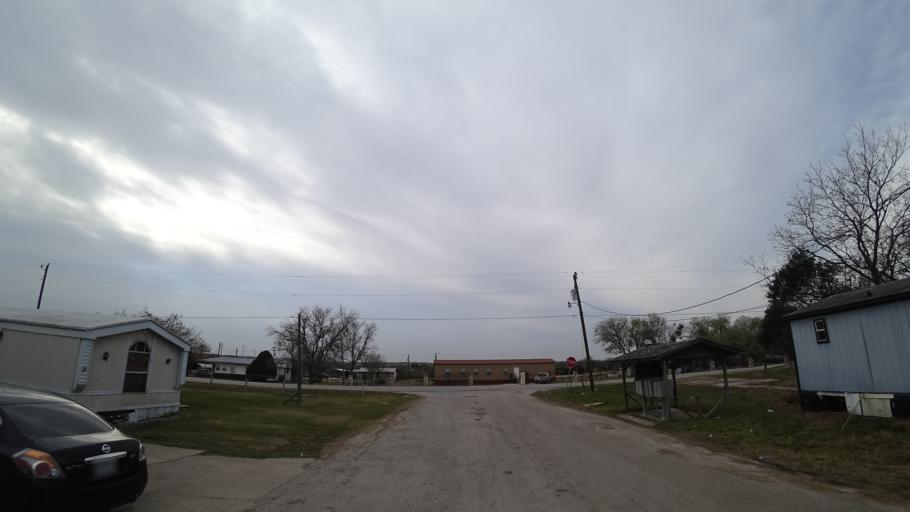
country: US
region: Texas
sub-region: Travis County
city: Garfield
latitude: 30.1516
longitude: -97.6642
